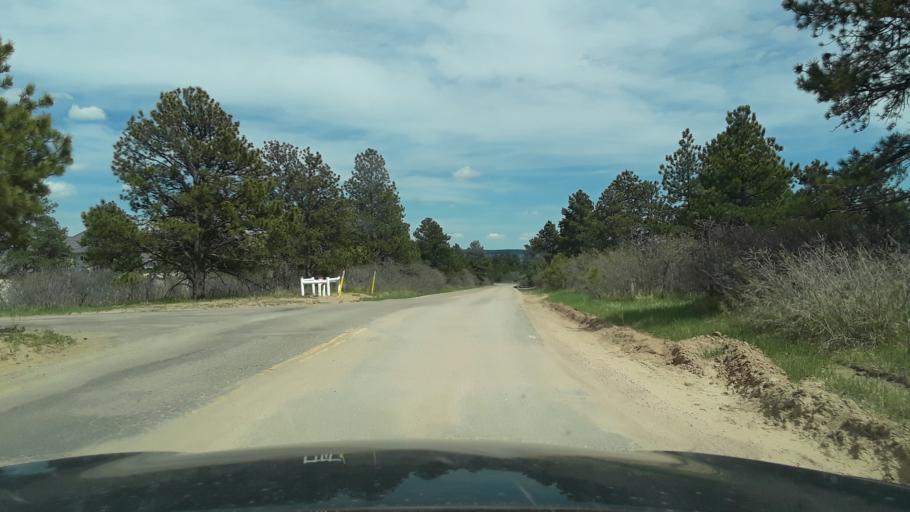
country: US
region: Colorado
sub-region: El Paso County
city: Monument
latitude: 39.0899
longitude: -104.8964
